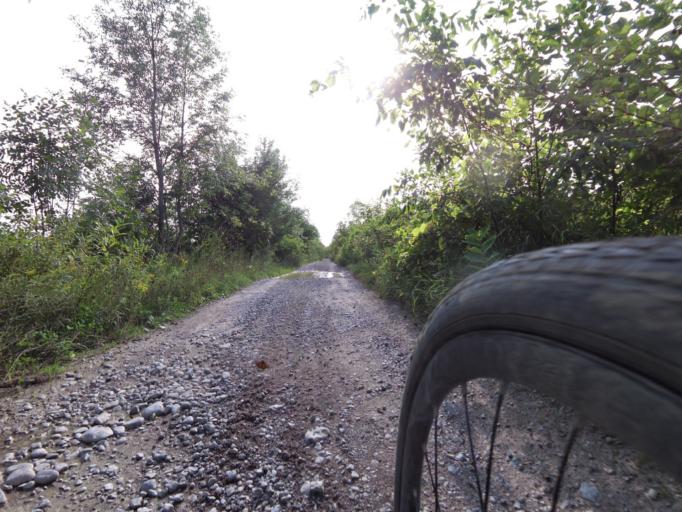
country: CA
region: Ontario
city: Quinte West
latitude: 44.0495
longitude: -77.6184
